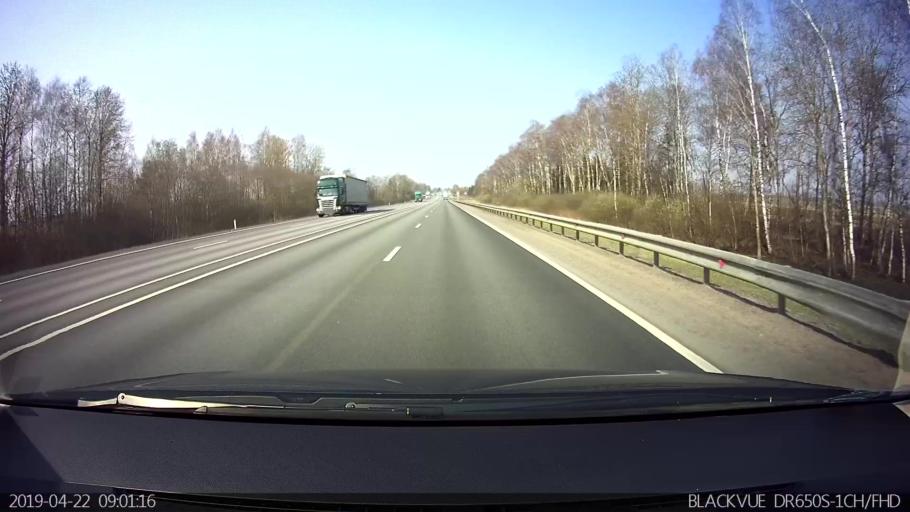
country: RU
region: Smolensk
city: Pechersk
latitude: 54.8613
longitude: 31.9191
